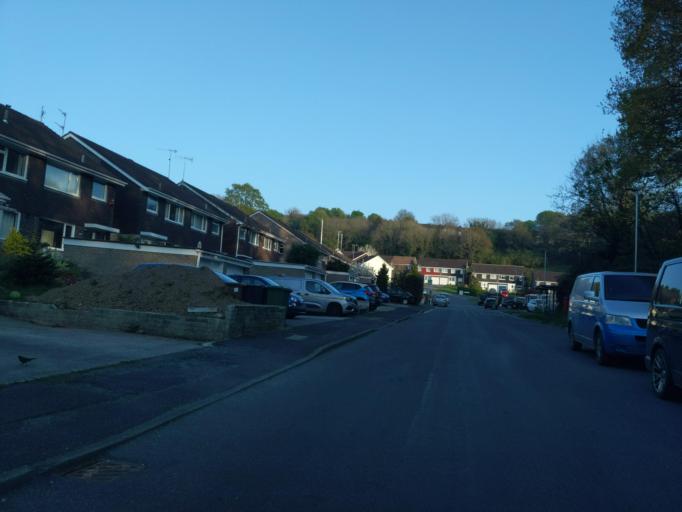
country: GB
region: England
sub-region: Plymouth
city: Plymstock
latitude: 50.3501
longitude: -4.0897
